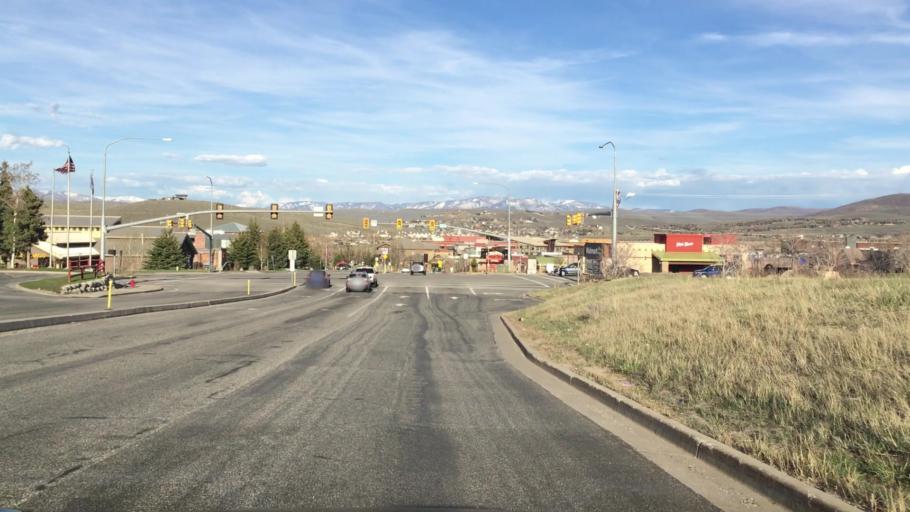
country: US
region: Utah
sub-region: Summit County
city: Snyderville
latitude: 40.7244
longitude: -111.5458
